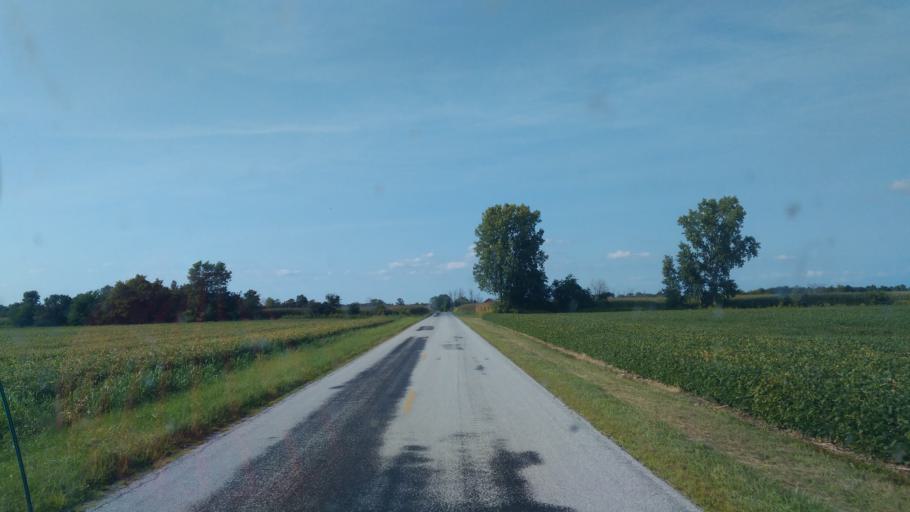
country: US
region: Ohio
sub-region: Hardin County
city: Kenton
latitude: 40.7295
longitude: -83.5738
